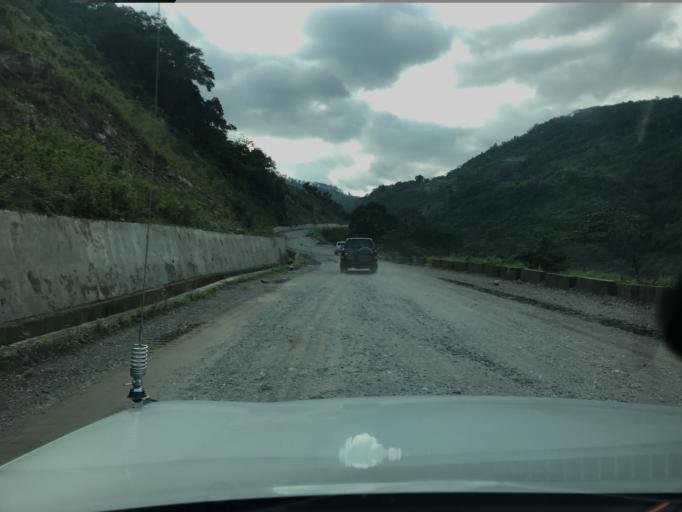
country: TL
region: Dili
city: Dili
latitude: -8.6394
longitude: 125.5091
